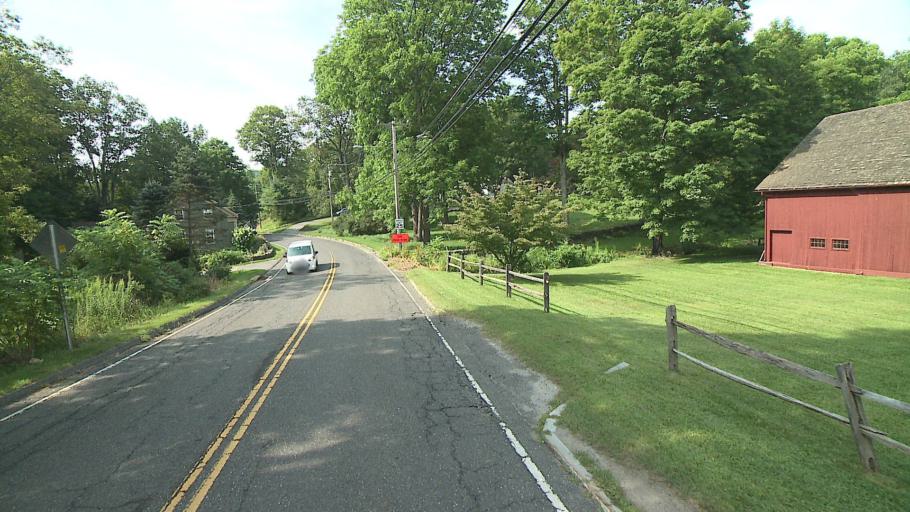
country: US
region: Connecticut
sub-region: Fairfield County
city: Sherman
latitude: 41.5774
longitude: -73.4984
